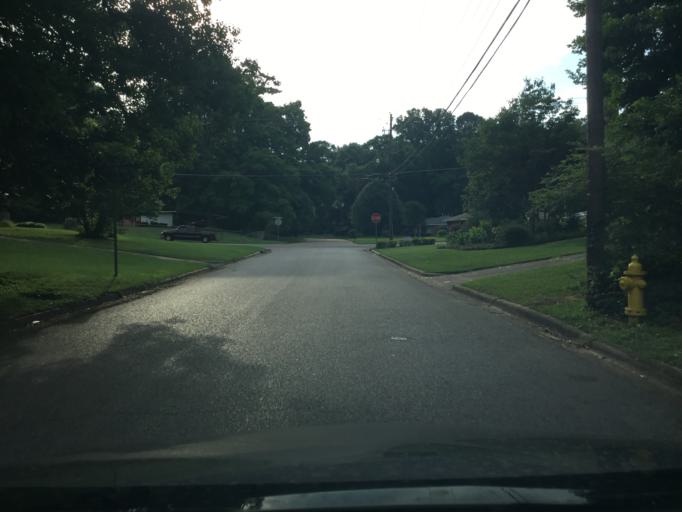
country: US
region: Alabama
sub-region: Montgomery County
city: Montgomery
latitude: 32.3747
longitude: -86.2572
